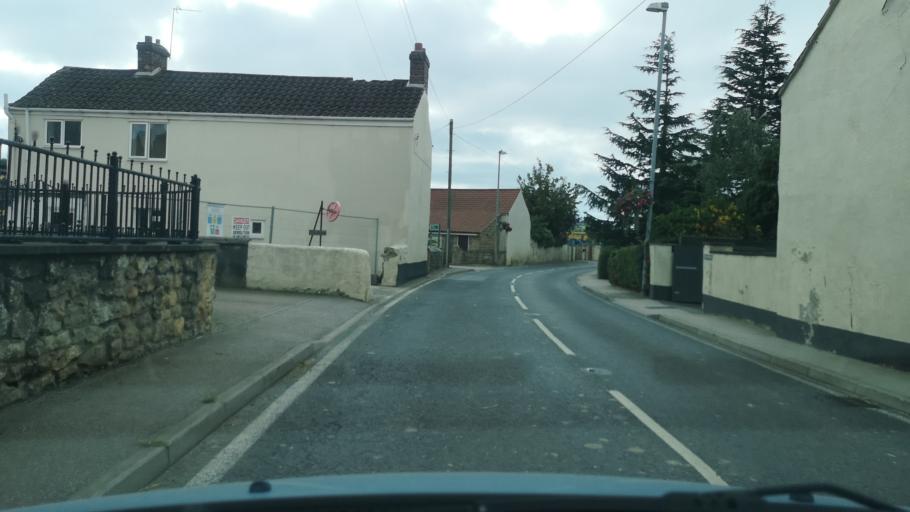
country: GB
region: England
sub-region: City and Borough of Wakefield
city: Badsworth
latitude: 53.6377
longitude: -1.2830
